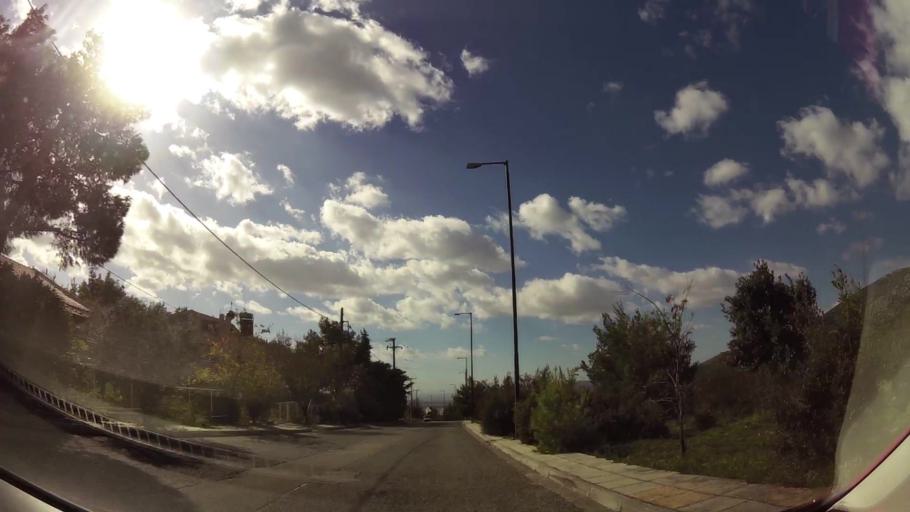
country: GR
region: Attica
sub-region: Nomarchia Anatolikis Attikis
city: Thrakomakedones
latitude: 38.1325
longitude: 23.7513
